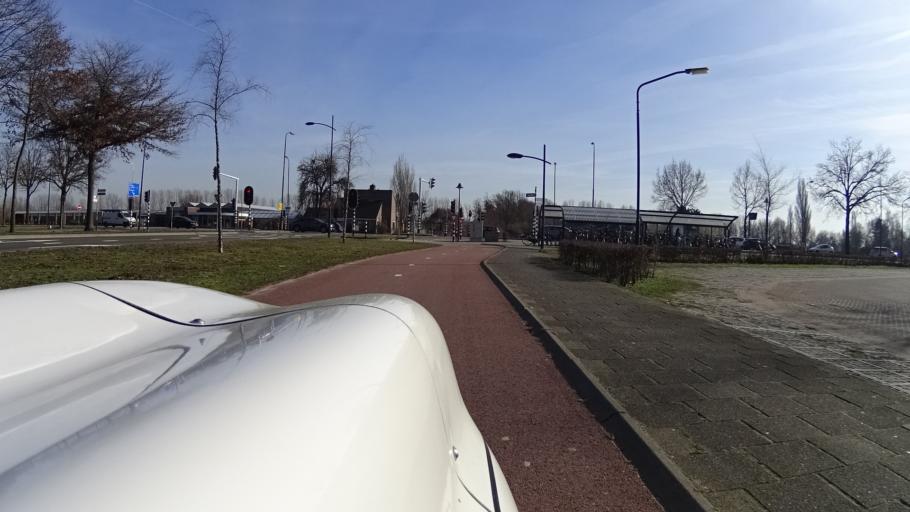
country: NL
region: North Brabant
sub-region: Gemeente Veghel
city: Veghel
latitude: 51.6213
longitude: 5.5653
